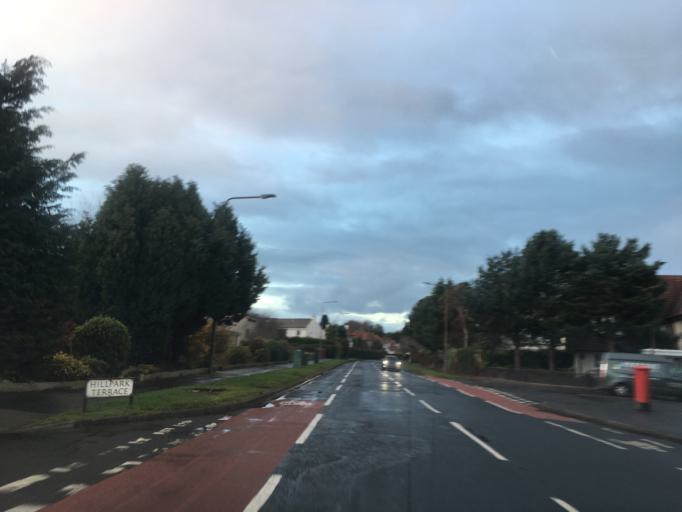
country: GB
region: Scotland
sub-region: Edinburgh
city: Colinton
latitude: 55.9589
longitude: -3.2693
